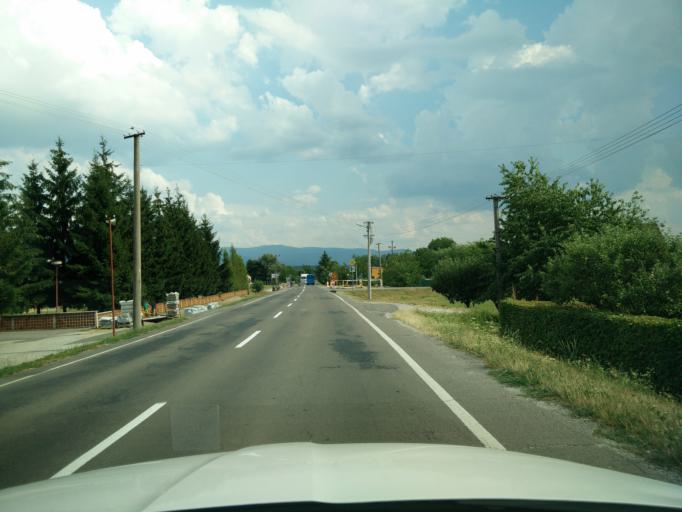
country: SK
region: Nitriansky
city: Novaky
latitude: 48.7469
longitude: 18.4985
